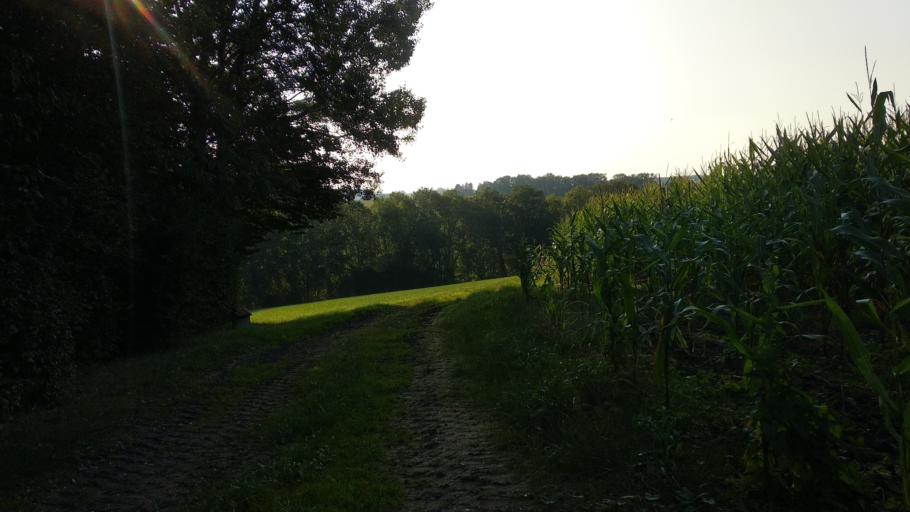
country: DE
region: Bavaria
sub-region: Upper Bavaria
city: Isen
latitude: 48.2006
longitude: 12.0689
